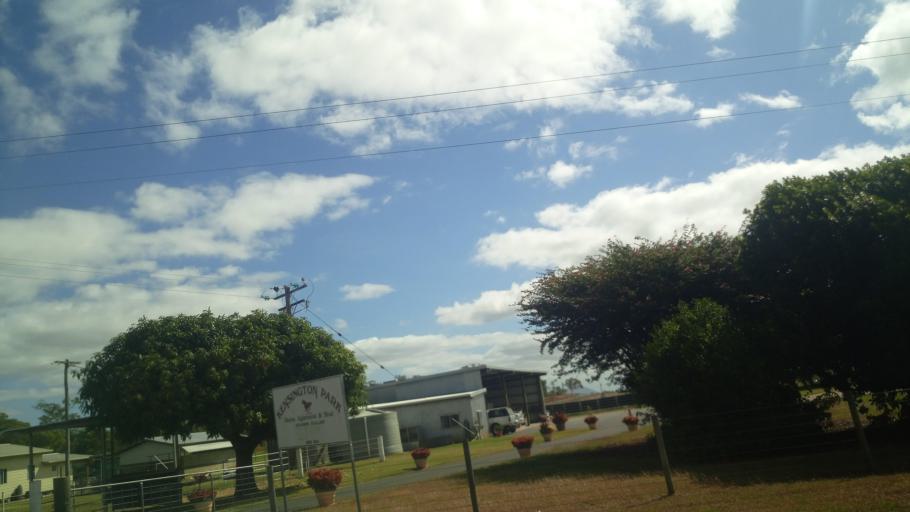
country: AU
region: Queensland
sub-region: Tablelands
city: Mareeba
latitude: -16.9748
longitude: 145.4573
